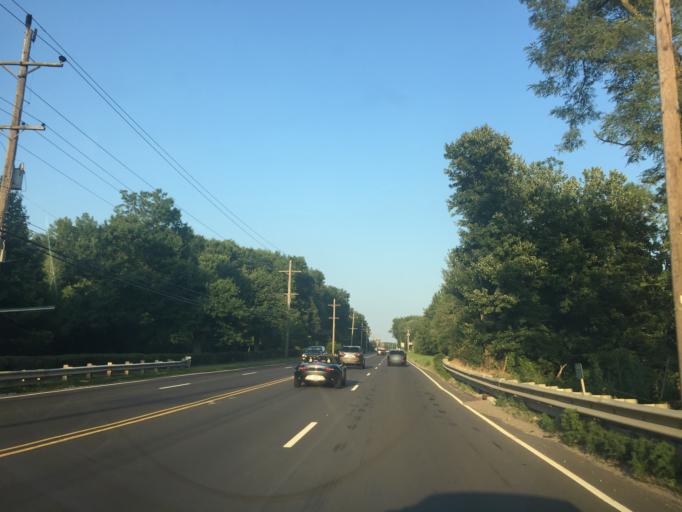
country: US
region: New Jersey
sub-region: Monmouth County
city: Farmingdale
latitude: 40.2185
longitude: -74.1172
